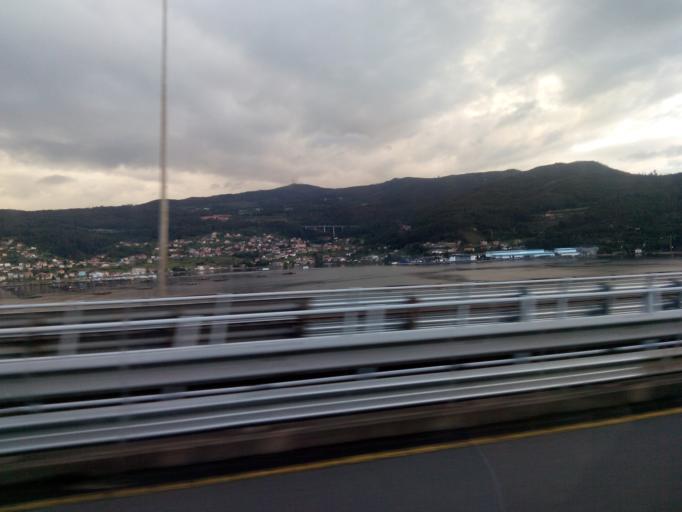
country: ES
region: Galicia
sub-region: Provincia de Pontevedra
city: Redondela
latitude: 42.2798
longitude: -8.6622
